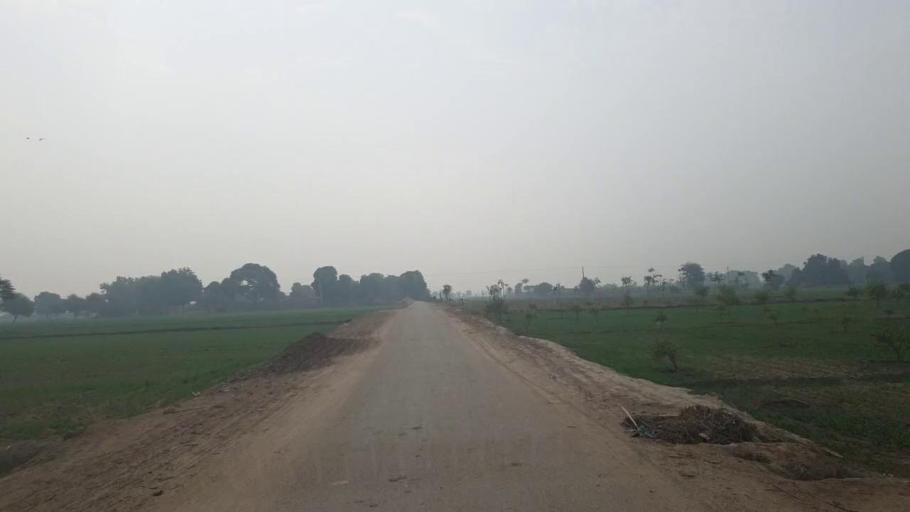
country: PK
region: Sindh
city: Tando Adam
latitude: 25.7063
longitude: 68.6263
